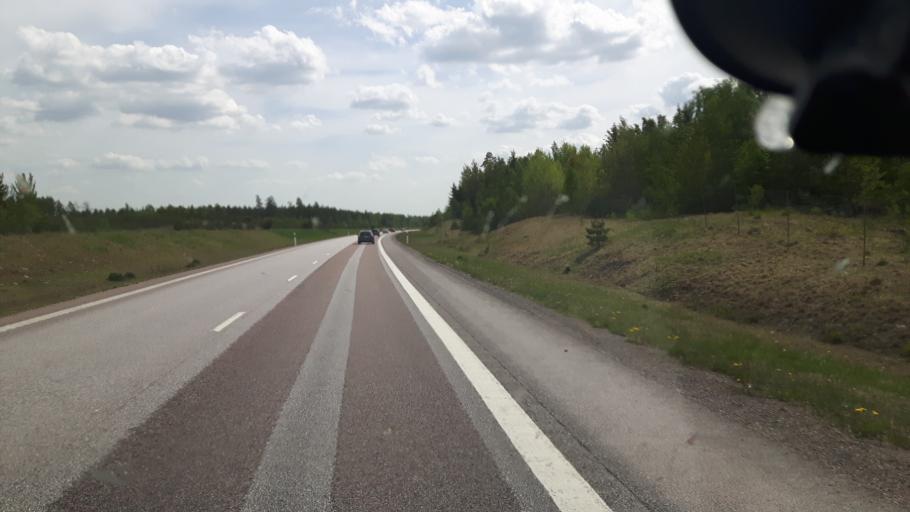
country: SE
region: Uppsala
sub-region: Osthammars Kommun
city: Bjorklinge
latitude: 60.0451
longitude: 17.6263
